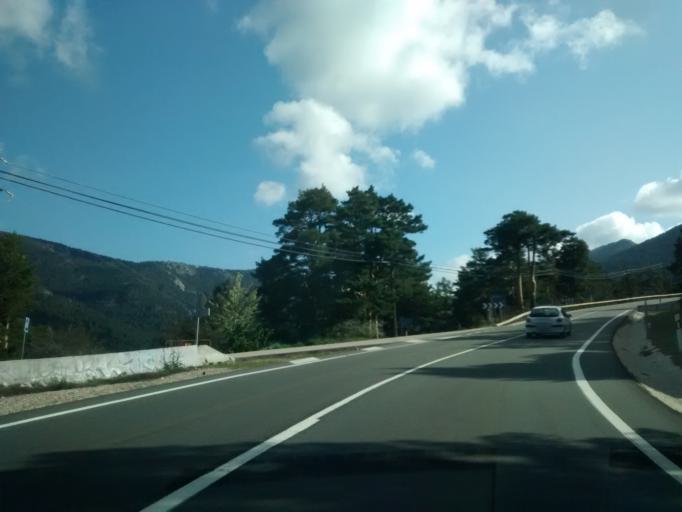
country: ES
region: Madrid
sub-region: Provincia de Madrid
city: Navacerrada
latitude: 40.7554
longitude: -4.0212
